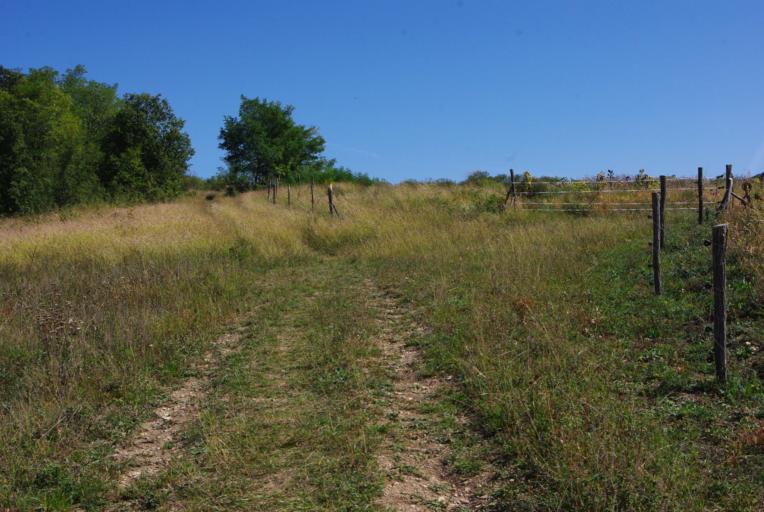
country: HU
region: Pest
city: Perbal
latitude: 47.5947
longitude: 18.7951
